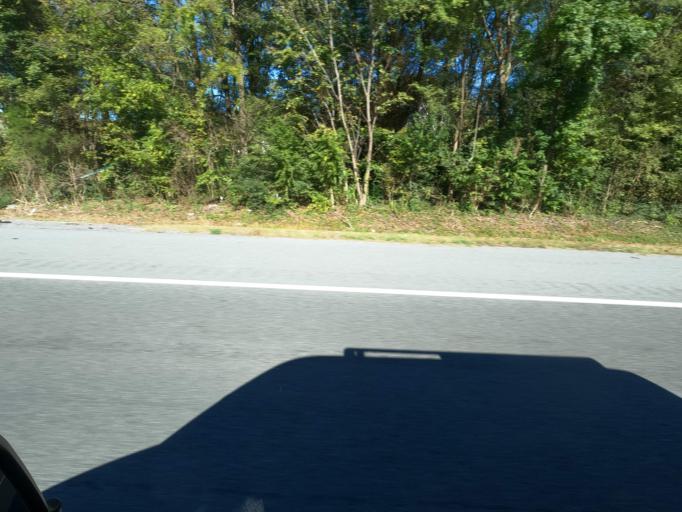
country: US
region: Tennessee
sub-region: Cheatham County
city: Kingston Springs
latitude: 36.0821
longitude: -87.1062
